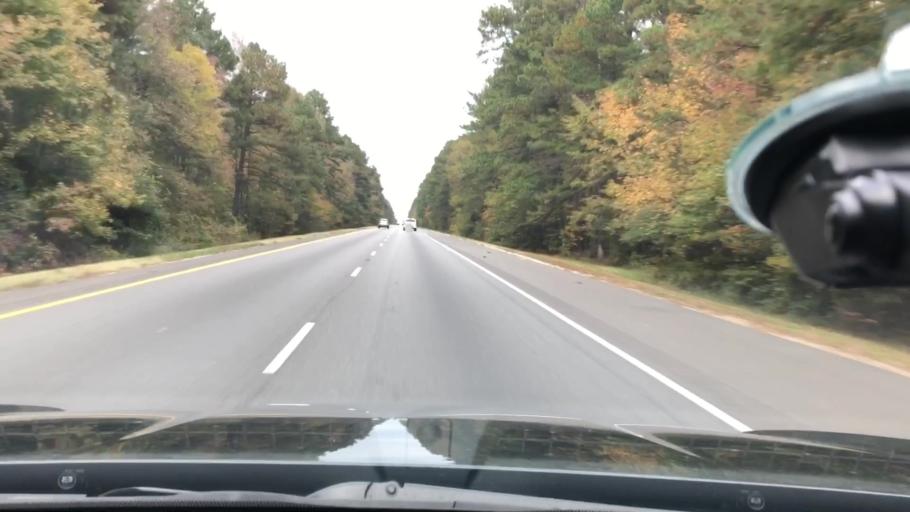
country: US
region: Arkansas
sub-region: Hot Spring County
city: Malvern
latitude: 34.2890
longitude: -92.9534
